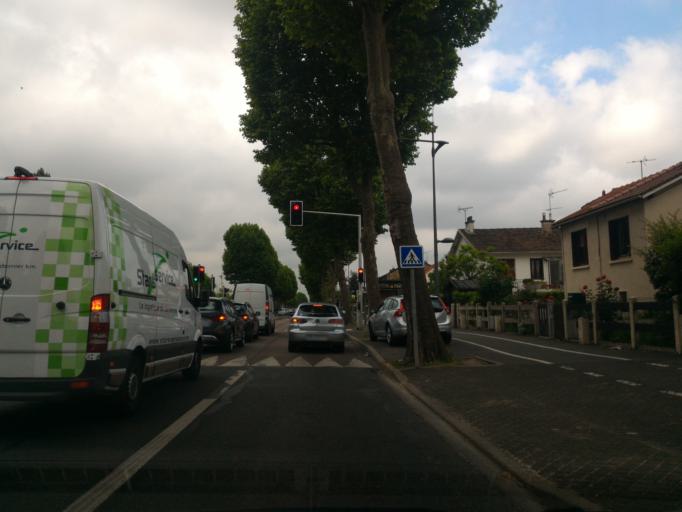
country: FR
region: Ile-de-France
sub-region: Departement du Val-de-Marne
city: Chevilly-Larue
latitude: 48.7701
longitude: 2.3378
